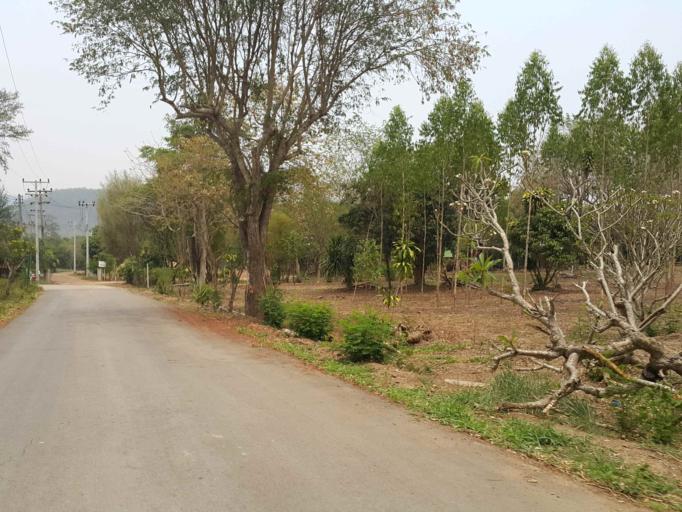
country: TH
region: Chiang Mai
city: San Sai
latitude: 18.9425
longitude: 99.0182
